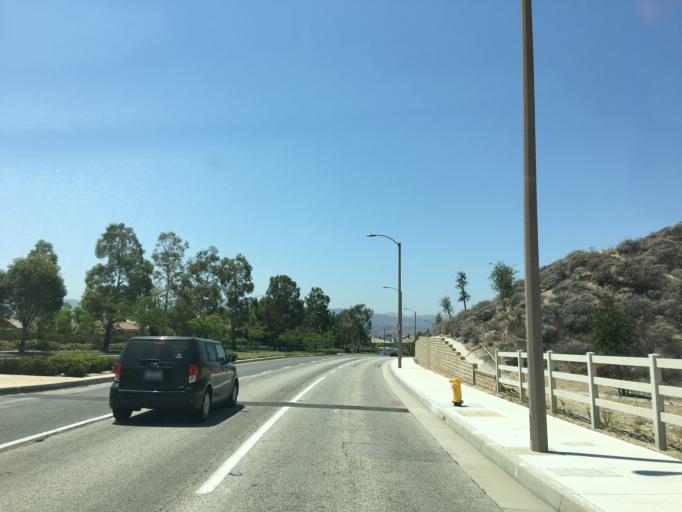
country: US
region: California
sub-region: Los Angeles County
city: Valencia
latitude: 34.4490
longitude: -118.5667
